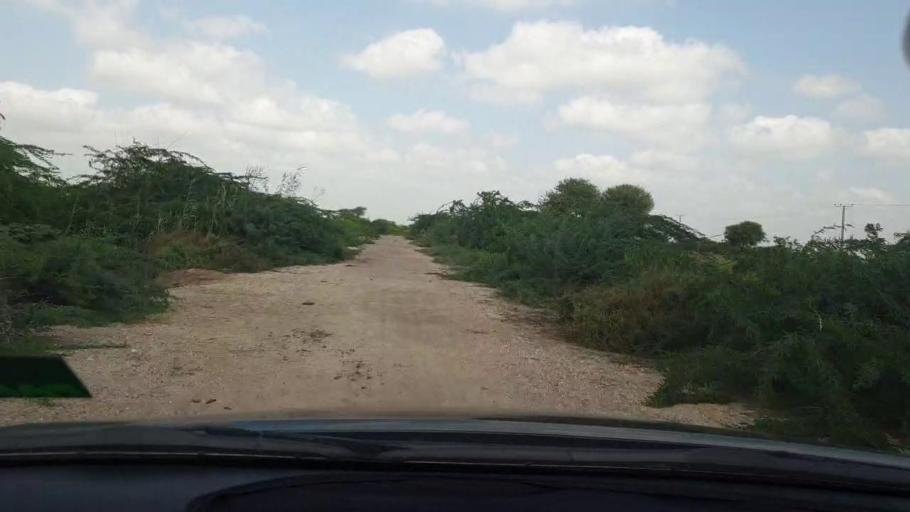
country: PK
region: Sindh
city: Tando Bago
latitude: 24.8560
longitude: 69.0334
